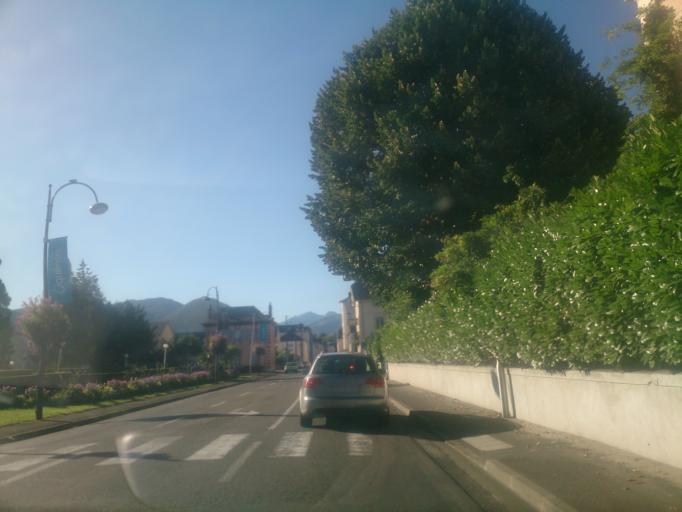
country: FR
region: Midi-Pyrenees
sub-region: Departement des Hautes-Pyrenees
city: Bagneres-de-Bigorre
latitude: 43.0691
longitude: 0.1464
